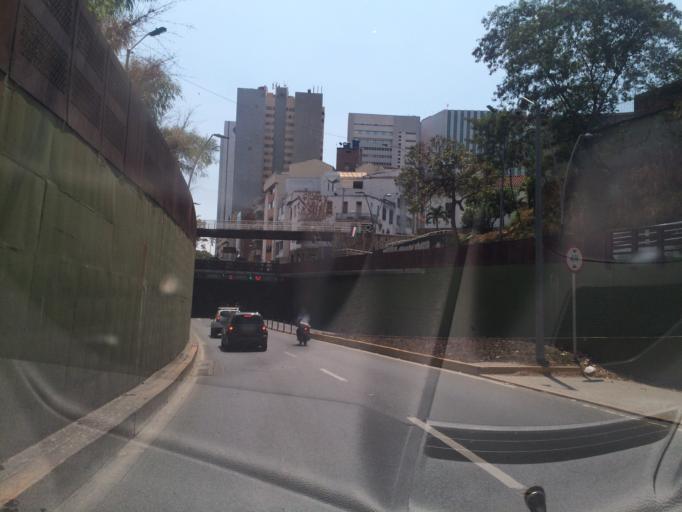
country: CO
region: Valle del Cauca
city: Cali
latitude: 3.4508
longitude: -76.5379
